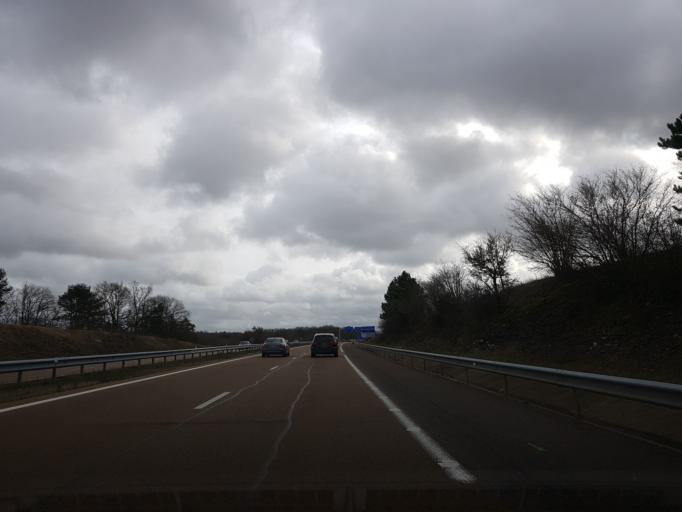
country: FR
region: Champagne-Ardenne
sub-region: Departement de la Haute-Marne
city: Rolampont
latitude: 47.9274
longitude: 5.2152
